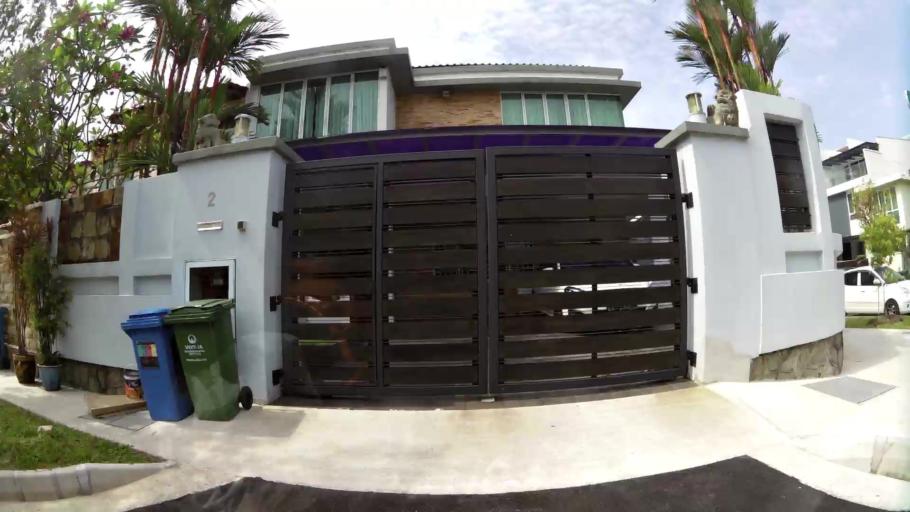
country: SG
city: Singapore
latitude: 1.3180
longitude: 103.7580
